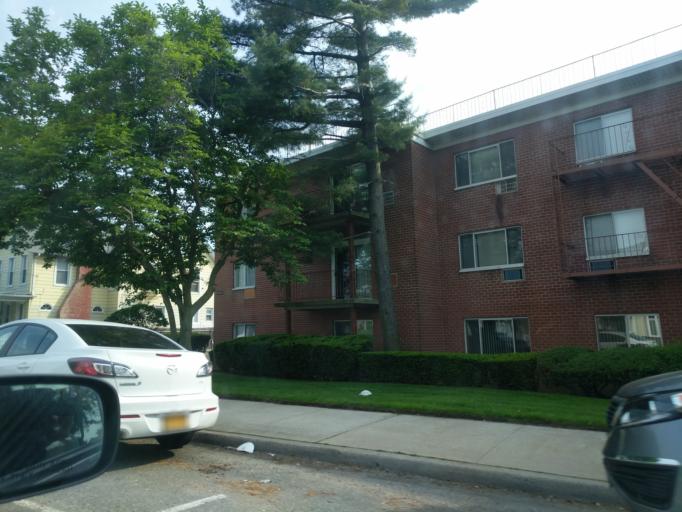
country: US
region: New York
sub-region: Nassau County
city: Rockville Centre
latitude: 40.6538
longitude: -73.6462
